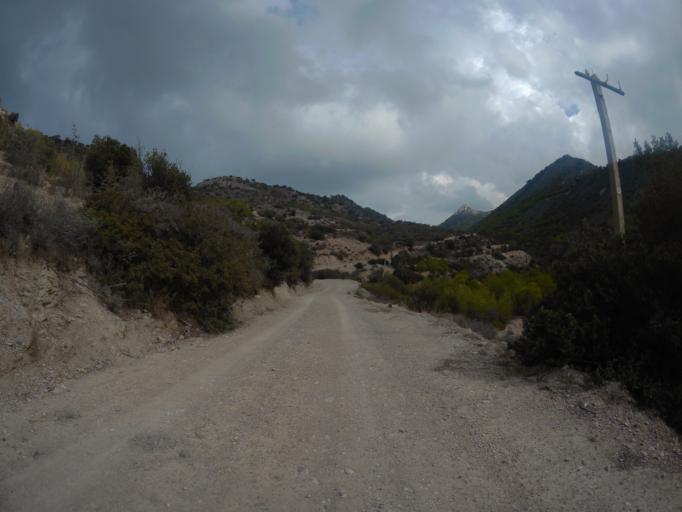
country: CY
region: Ammochostos
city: Lefkonoiko
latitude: 35.3483
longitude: 33.7283
